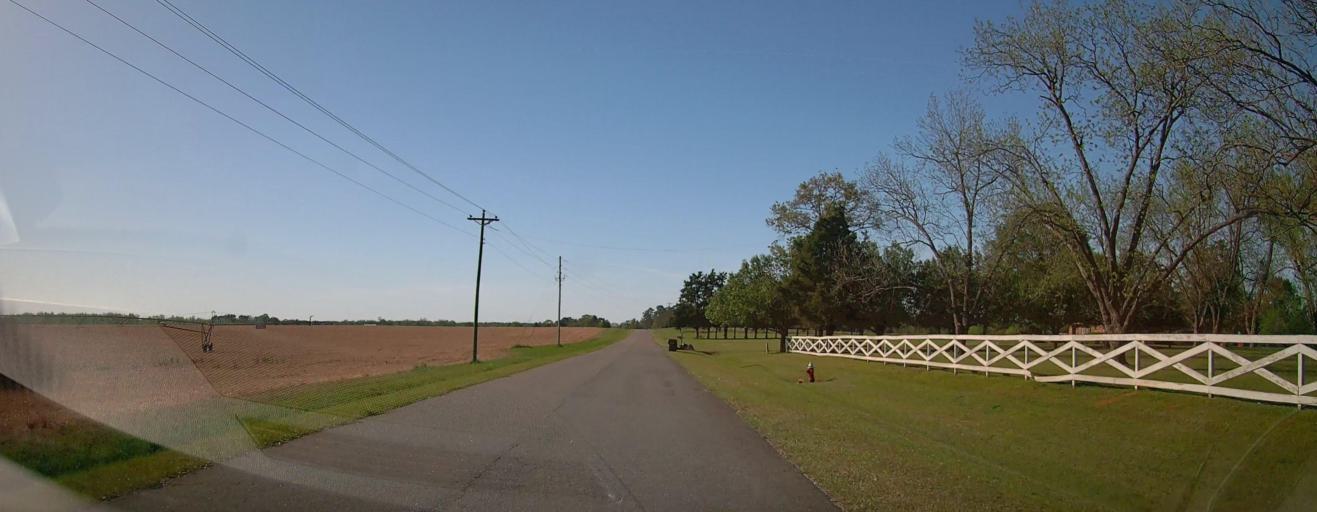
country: US
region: Georgia
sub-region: Houston County
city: Perry
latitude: 32.4316
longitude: -83.7831
